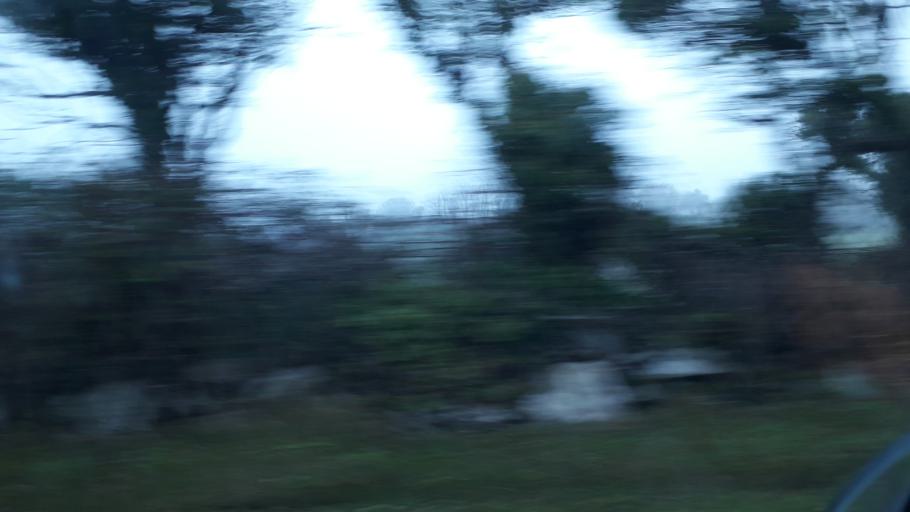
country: IE
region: Ulster
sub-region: County Donegal
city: Newtown Cunningham
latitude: 55.0917
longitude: -7.5522
